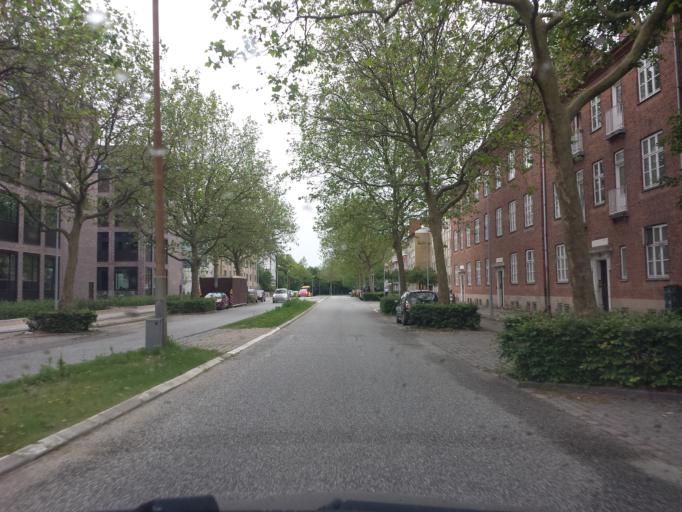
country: DK
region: Capital Region
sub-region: Lyngby-Tarbaek Kommune
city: Kongens Lyngby
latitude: 55.7651
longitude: 12.5099
